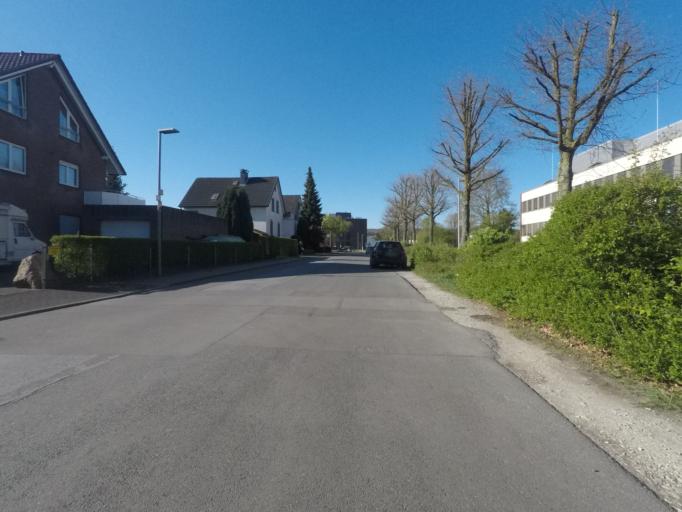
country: DE
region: North Rhine-Westphalia
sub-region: Regierungsbezirk Detmold
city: Bielefeld
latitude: 52.0093
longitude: 8.5907
